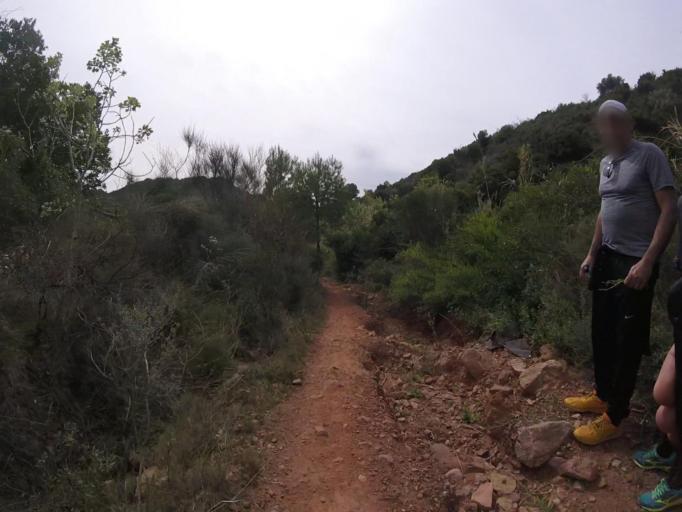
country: ES
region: Valencia
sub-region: Provincia de Castello
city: Benicassim
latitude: 40.0743
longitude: 0.0345
